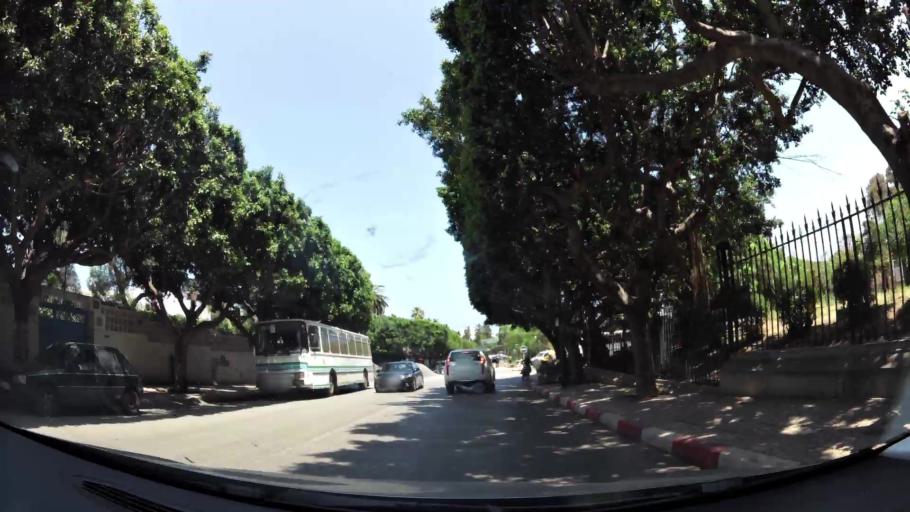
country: MA
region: Rabat-Sale-Zemmour-Zaer
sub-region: Rabat
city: Rabat
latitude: 34.0130
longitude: -6.8263
